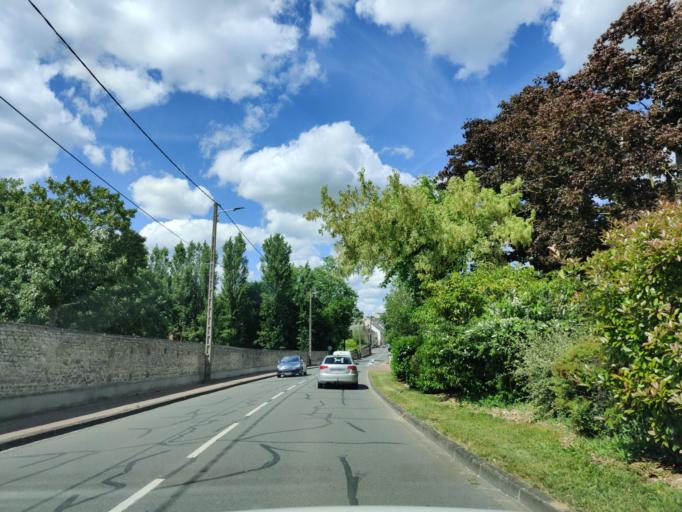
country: FR
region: Centre
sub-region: Departement du Loiret
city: Pithiviers
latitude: 48.1656
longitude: 2.2563
